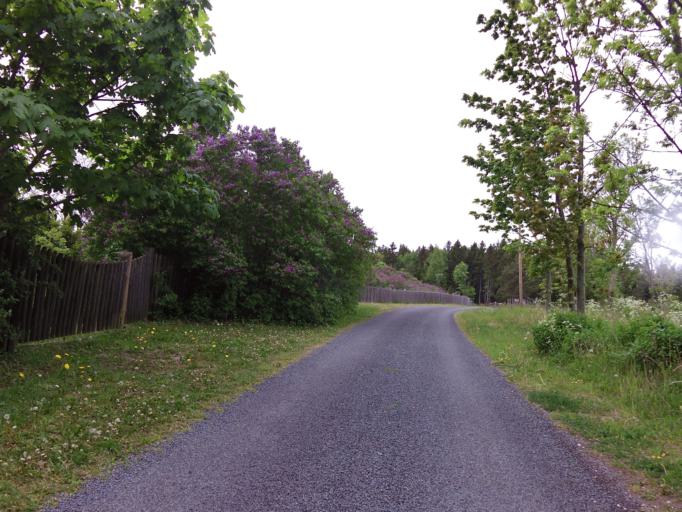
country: EE
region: Harju
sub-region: Paldiski linn
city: Paldiski
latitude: 59.2563
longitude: 23.7471
